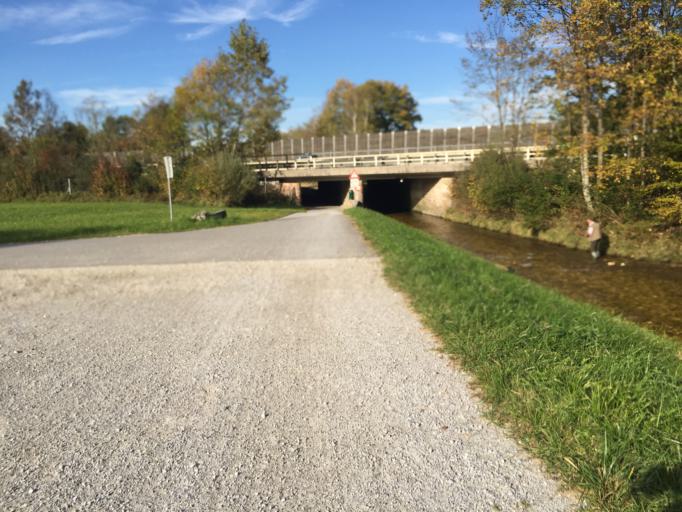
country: AT
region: Salzburg
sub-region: Politischer Bezirk Salzburg-Umgebung
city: Grodig
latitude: 47.7620
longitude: 12.9996
